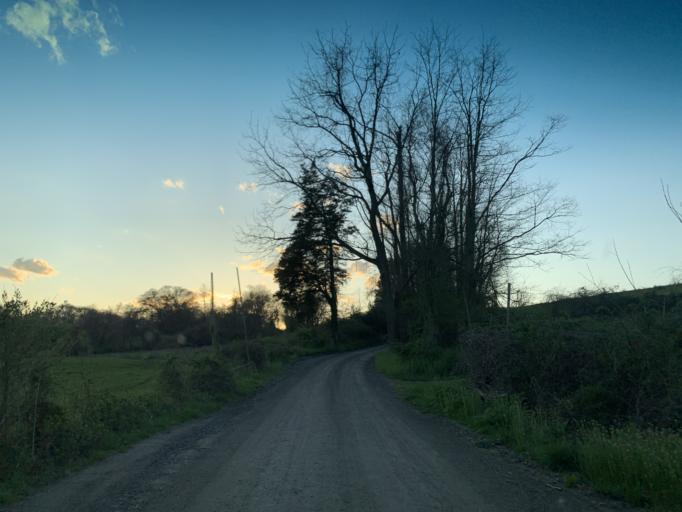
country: US
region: Maryland
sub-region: Harford County
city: Bel Air North
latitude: 39.6189
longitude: -76.3640
